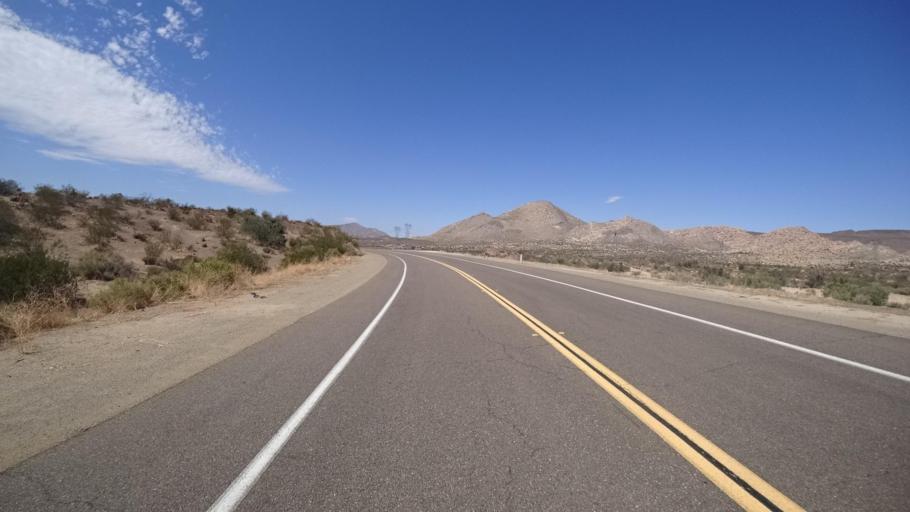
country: MX
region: Baja California
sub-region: Tecate
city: Cereso del Hongo
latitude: 32.6250
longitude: -116.1589
